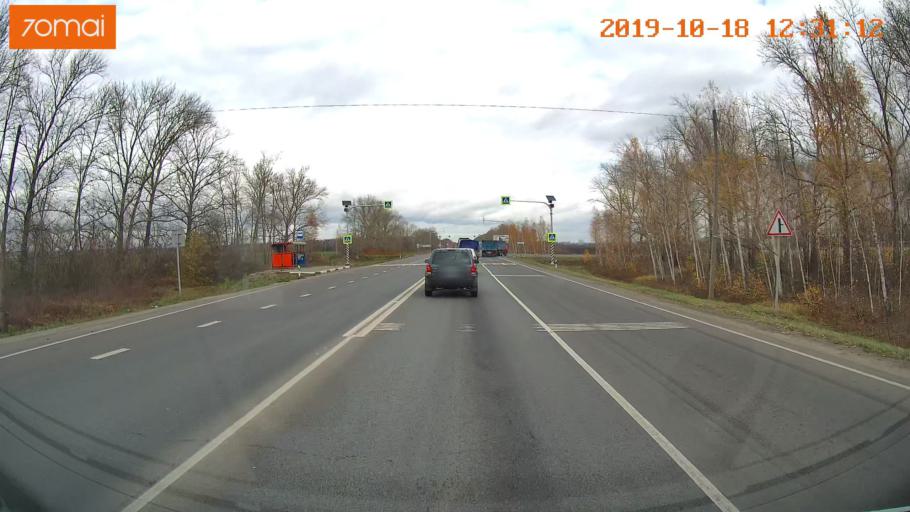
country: RU
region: Rjazan
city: Ryazan'
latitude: 54.5915
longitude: 39.6094
